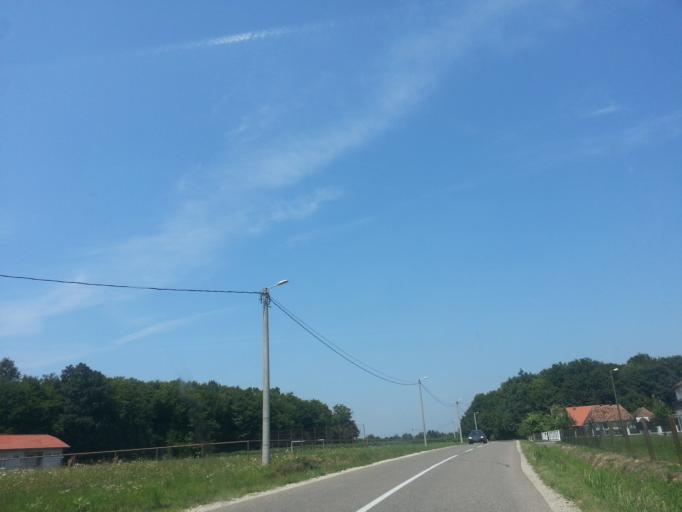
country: BA
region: Brcko
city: Brcko
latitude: 44.7971
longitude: 18.8428
